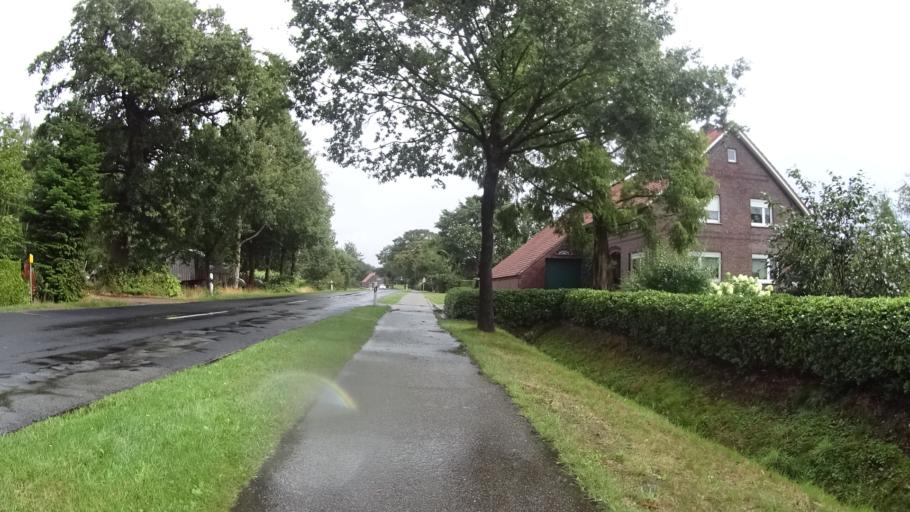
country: DE
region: Lower Saxony
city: Firrel
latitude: 53.3358
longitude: 7.6752
